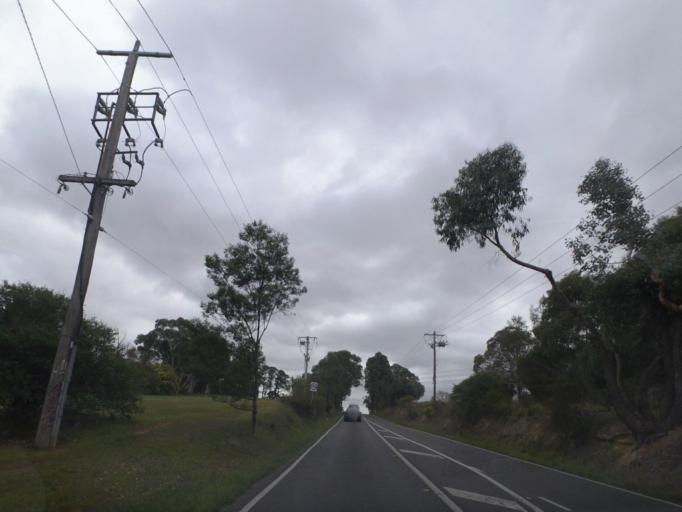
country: AU
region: Victoria
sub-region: Nillumbik
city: Eltham North
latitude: -37.6853
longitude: 145.1432
